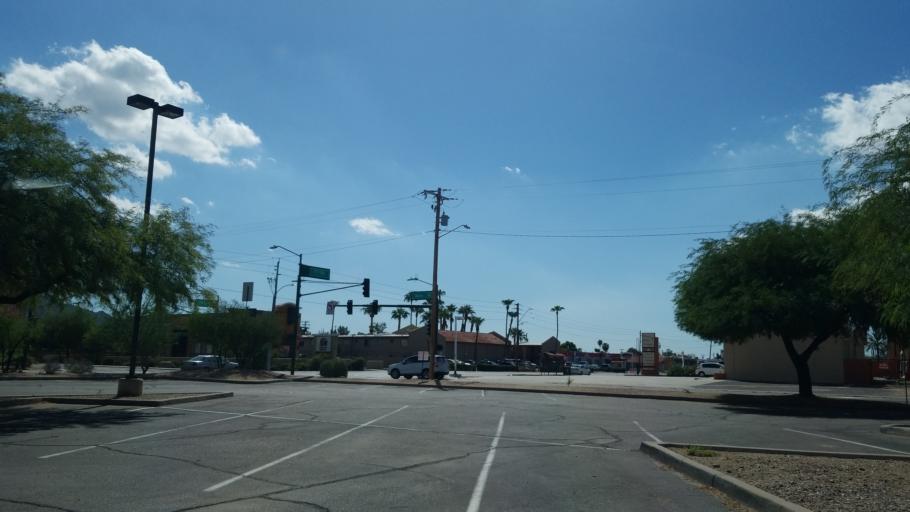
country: US
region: Arizona
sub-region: Maricopa County
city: Phoenix
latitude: 33.5645
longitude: -112.0658
